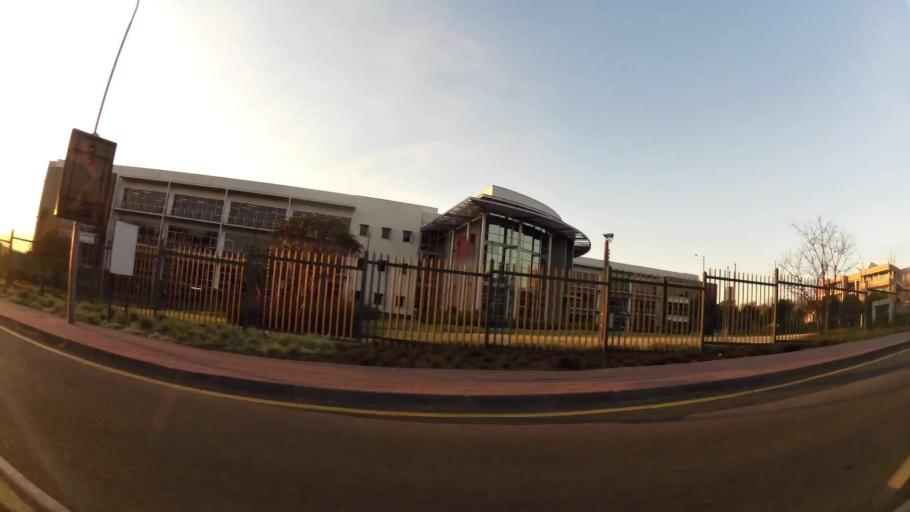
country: ZA
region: Gauteng
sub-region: City of Johannesburg Metropolitan Municipality
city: Modderfontein
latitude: -26.0661
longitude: 28.0811
